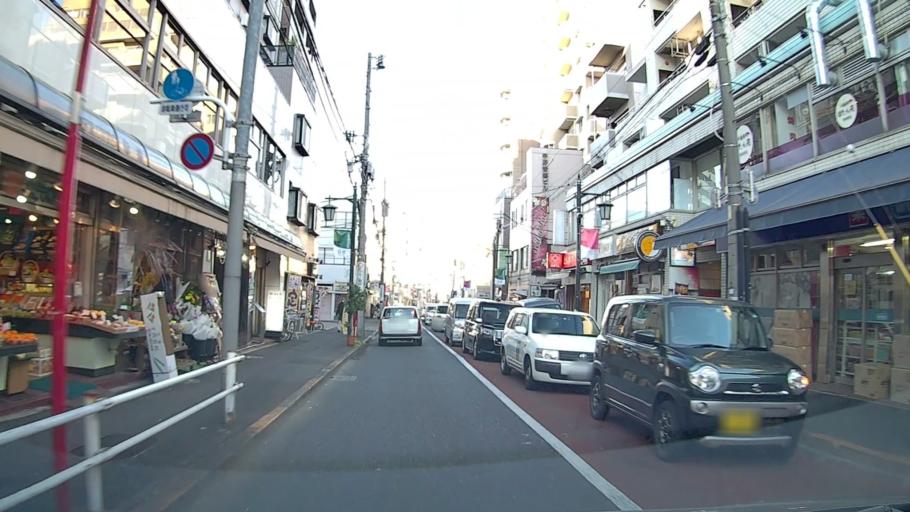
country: JP
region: Tokyo
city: Tokyo
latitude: 35.6976
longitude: 139.6709
